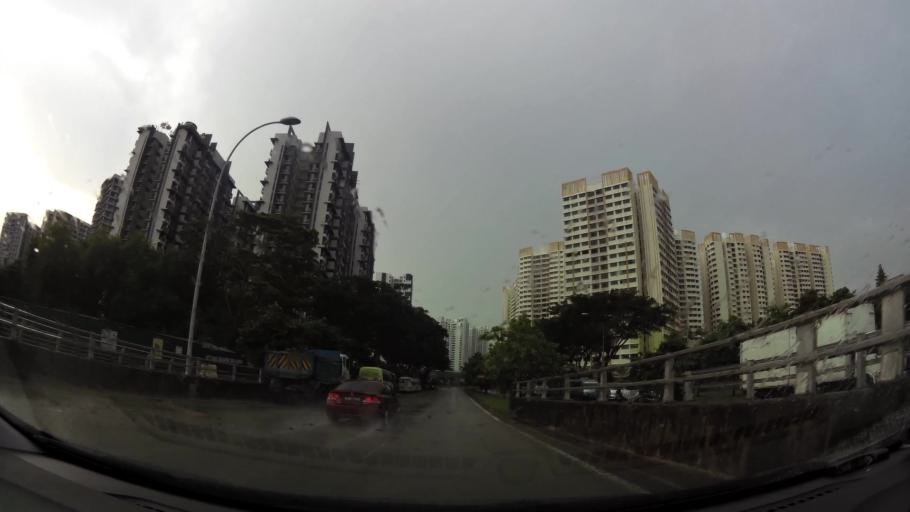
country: MY
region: Johor
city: Kampung Pasir Gudang Baru
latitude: 1.3952
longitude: 103.8828
